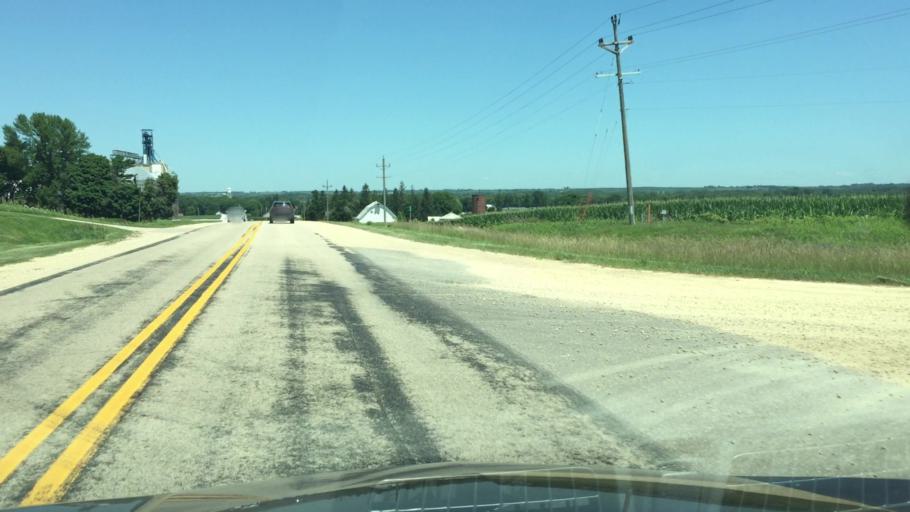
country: US
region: Iowa
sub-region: Cedar County
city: Mechanicsville
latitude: 41.9832
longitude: -91.1416
